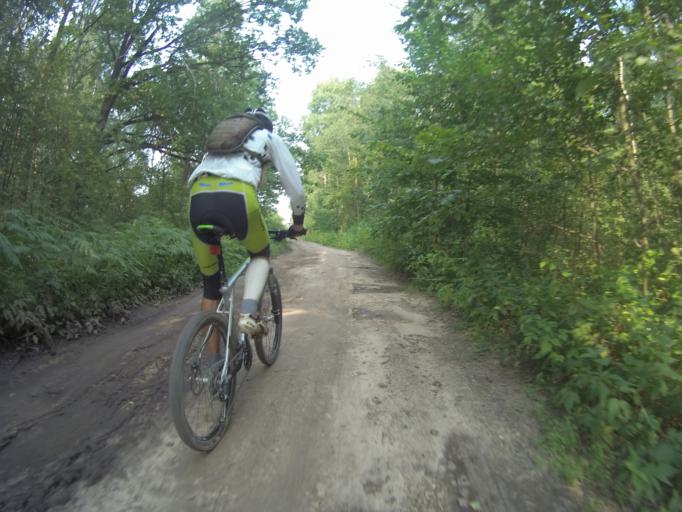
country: RU
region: Vladimir
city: Vorsha
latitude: 56.0101
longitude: 40.1224
